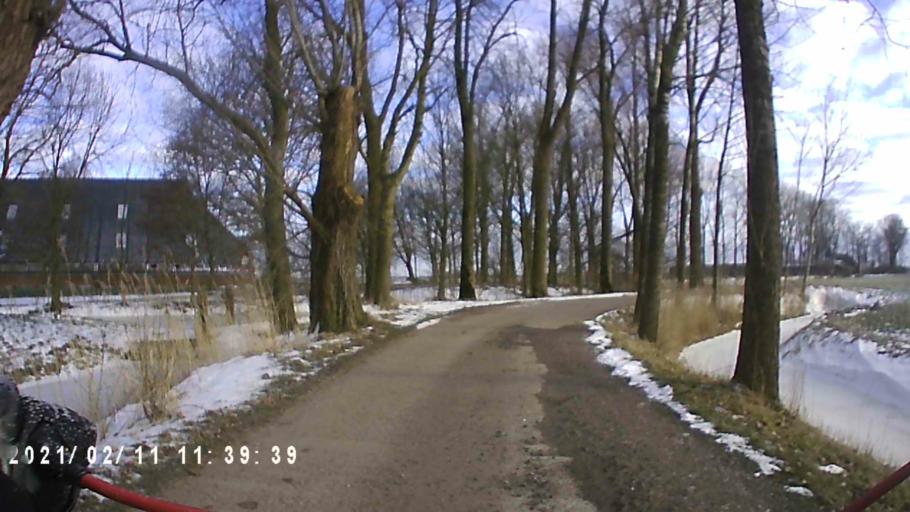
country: NL
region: Groningen
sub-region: Gemeente Zuidhorn
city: Aduard
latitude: 53.2844
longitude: 6.4600
